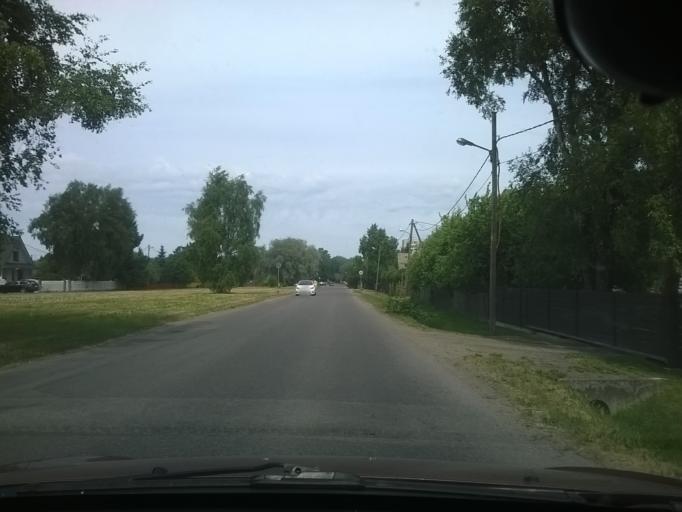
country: EE
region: Harju
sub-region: Tallinna linn
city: Tallinn
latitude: 59.4263
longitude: 24.6899
